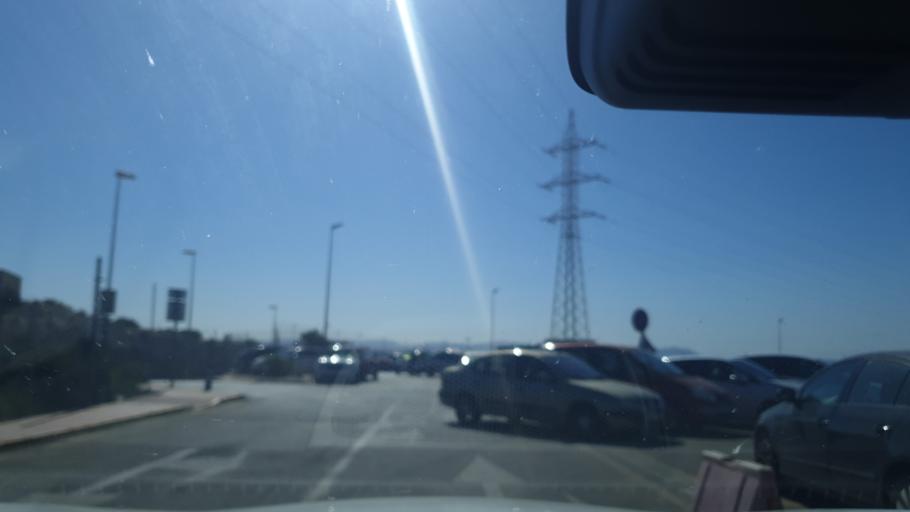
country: ES
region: Andalusia
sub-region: Provincia de Almeria
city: Huercal de Almeria
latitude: 36.8626
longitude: -2.4394
